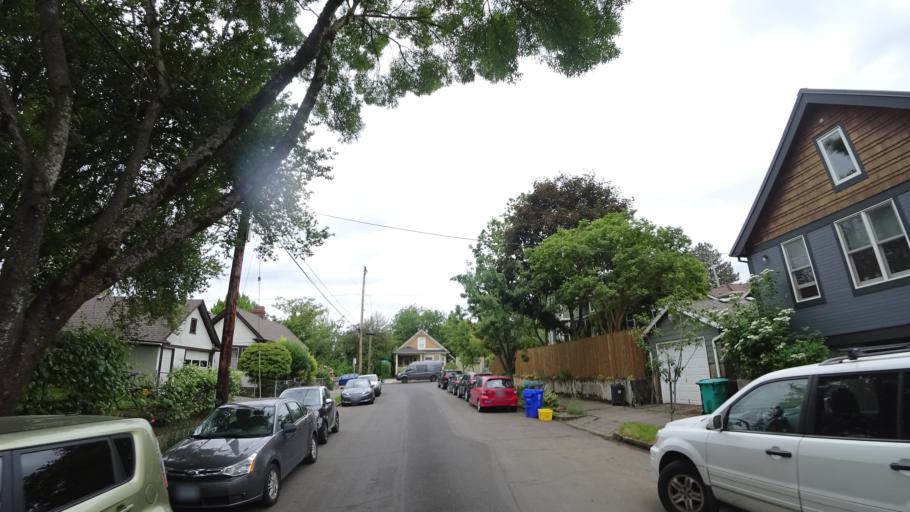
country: US
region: Oregon
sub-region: Multnomah County
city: Lents
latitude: 45.5155
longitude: -122.6141
